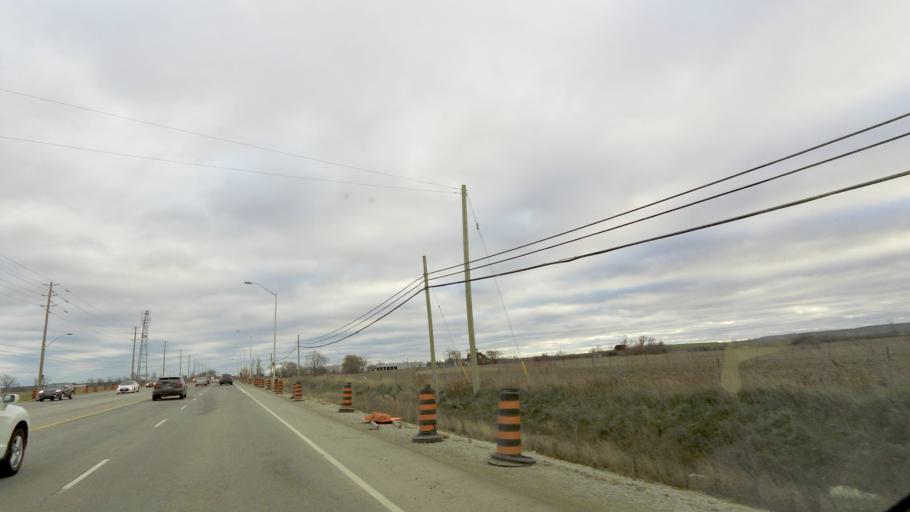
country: CA
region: Ontario
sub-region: Halton
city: Milton
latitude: 43.4857
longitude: -79.8335
